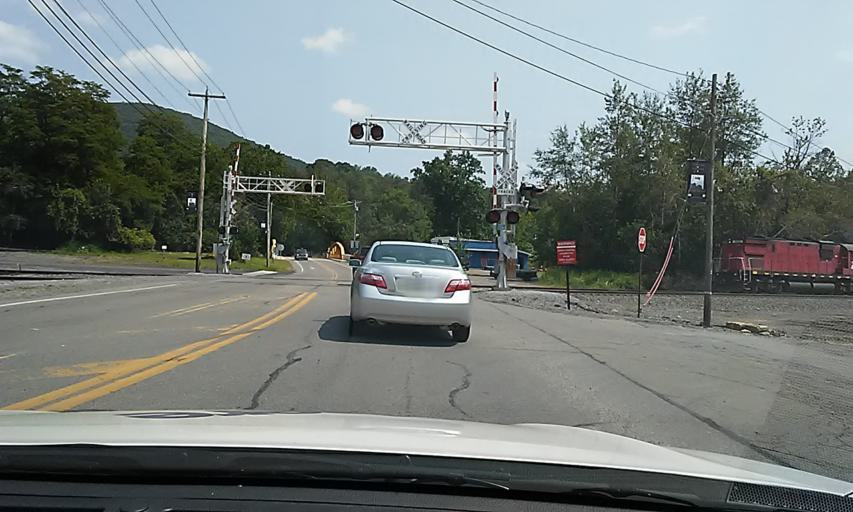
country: US
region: Pennsylvania
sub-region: Cameron County
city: Emporium
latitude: 41.5088
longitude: -78.2234
